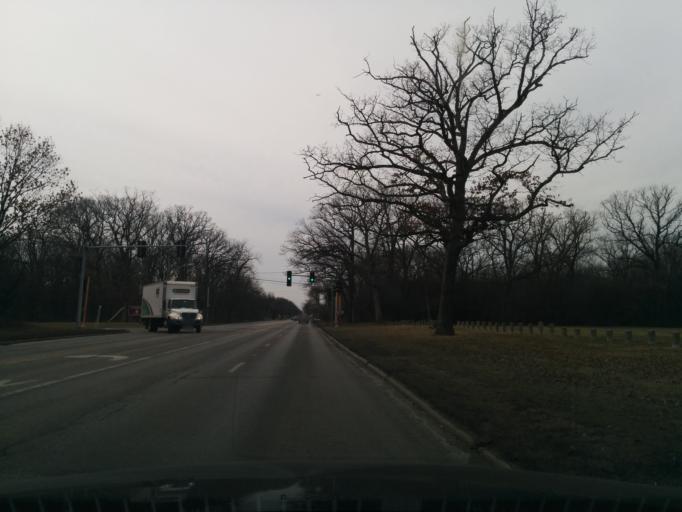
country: US
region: Illinois
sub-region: Cook County
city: Westchester
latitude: 41.8341
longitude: -87.8802
